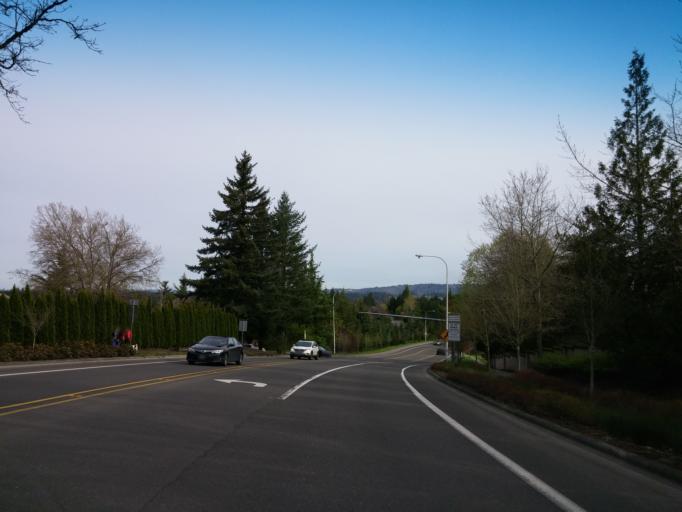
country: US
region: Oregon
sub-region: Washington County
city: Cedar Mill
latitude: 45.5361
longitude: -122.8120
